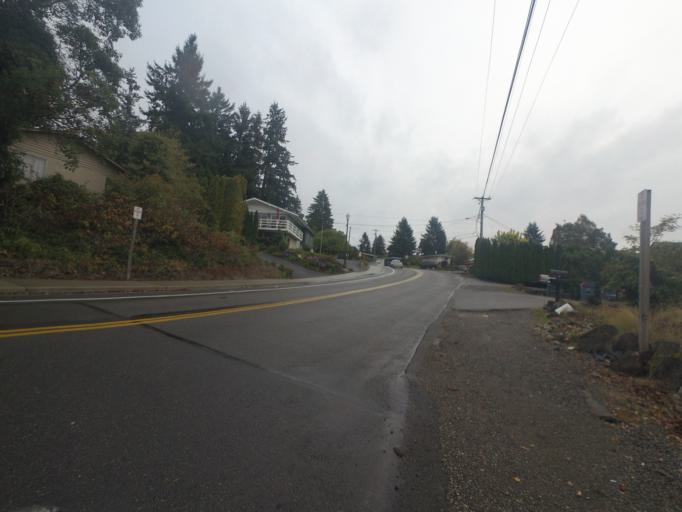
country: US
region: Washington
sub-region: Pierce County
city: University Place
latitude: 47.2205
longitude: -122.5516
